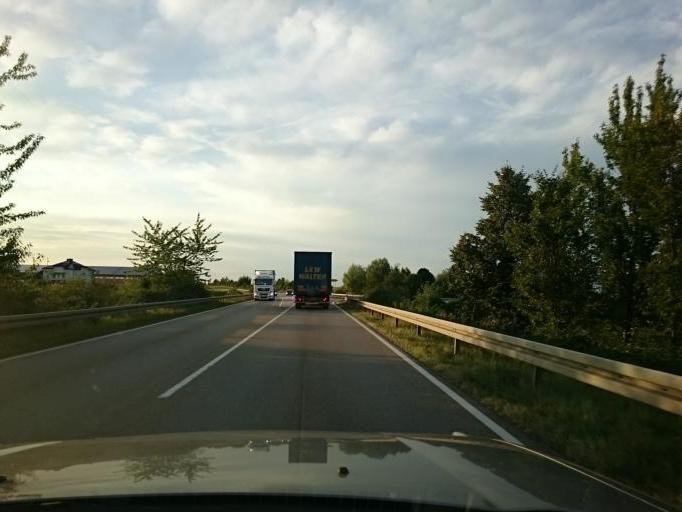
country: DE
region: Bavaria
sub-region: Lower Bavaria
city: Oberschneiding
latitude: 48.7673
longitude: 12.6600
